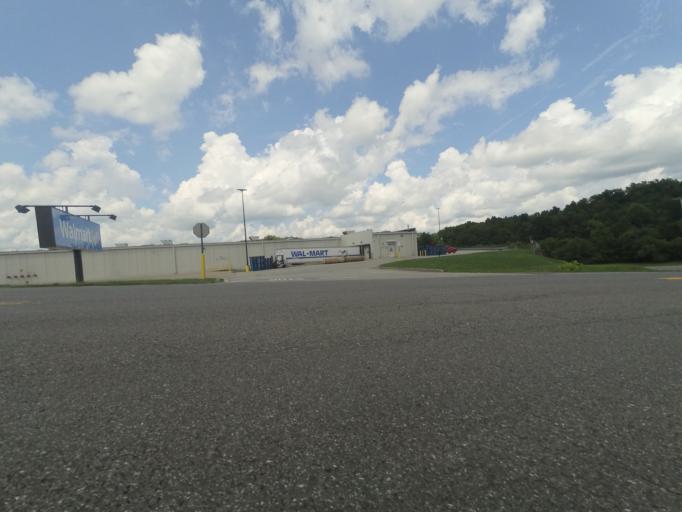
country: US
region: West Virginia
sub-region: Cabell County
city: Pea Ridge
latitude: 38.4061
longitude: -82.3749
